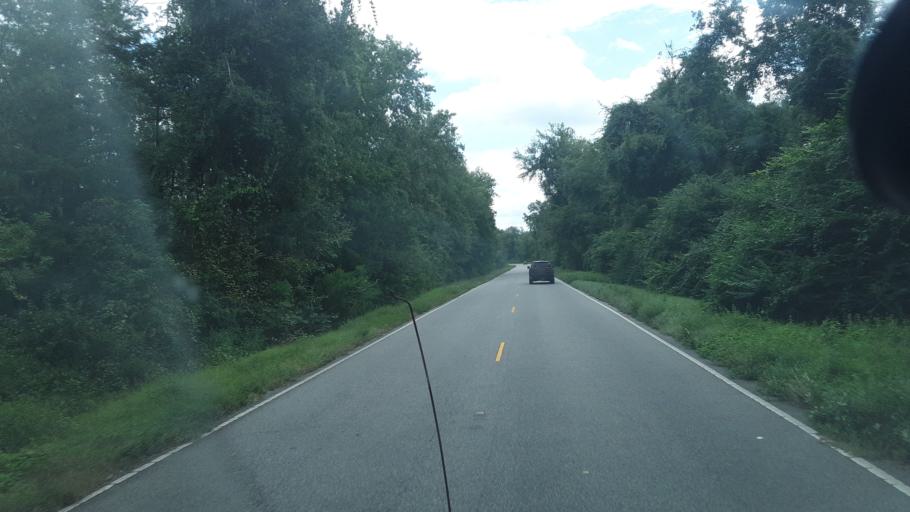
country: US
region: North Carolina
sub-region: Robeson County
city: Fairmont
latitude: 34.3492
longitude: -79.0795
